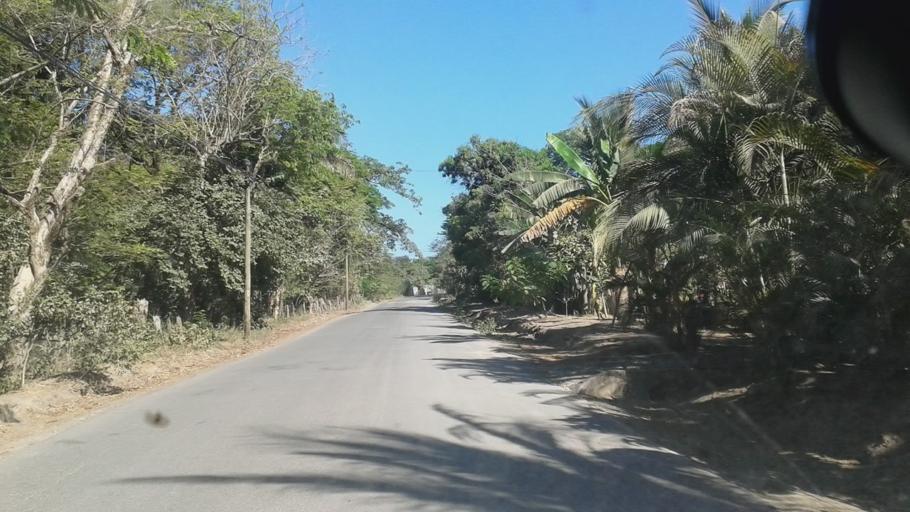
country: CR
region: Guanacaste
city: Samara
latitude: 9.9086
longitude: -85.5983
